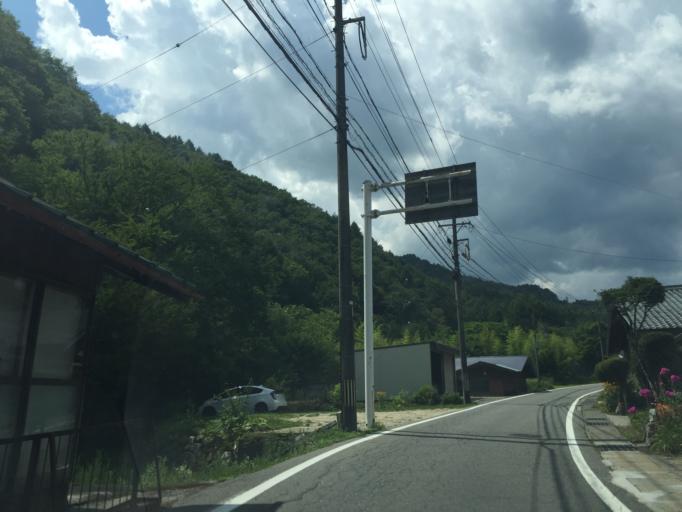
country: JP
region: Nagano
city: Iida
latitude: 35.3766
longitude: 137.6873
